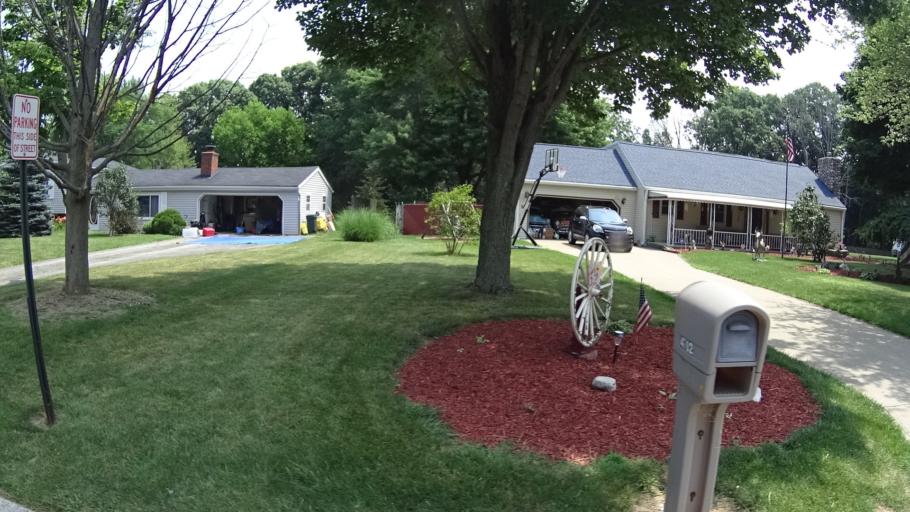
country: US
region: Ohio
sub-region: Lorain County
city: Vermilion
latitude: 41.4177
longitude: -82.3823
